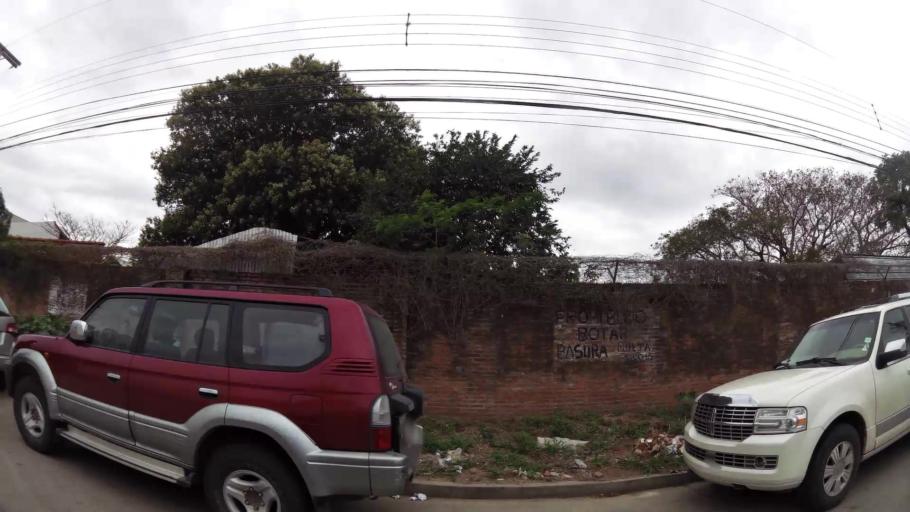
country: BO
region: Santa Cruz
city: Santa Cruz de la Sierra
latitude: -17.7603
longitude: -63.1924
